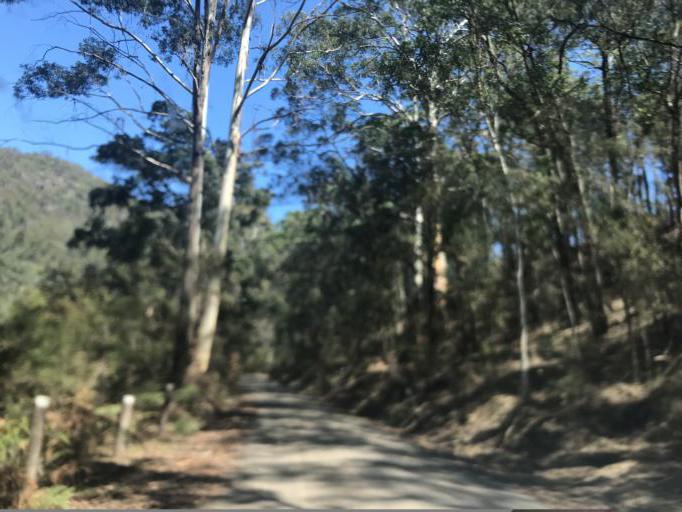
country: AU
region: New South Wales
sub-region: Wyong Shire
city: Little Jilliby
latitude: -33.1965
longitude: 151.0193
